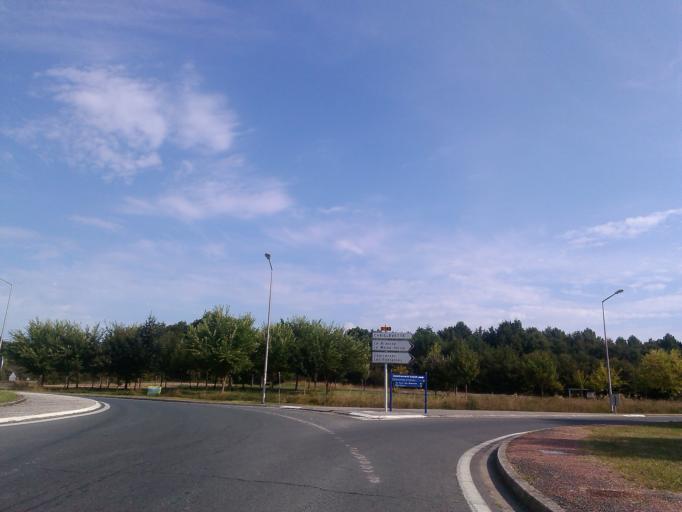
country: FR
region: Poitou-Charentes
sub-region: Departement de la Charente-Maritime
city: Chaillevette
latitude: 45.7210
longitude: -1.0793
